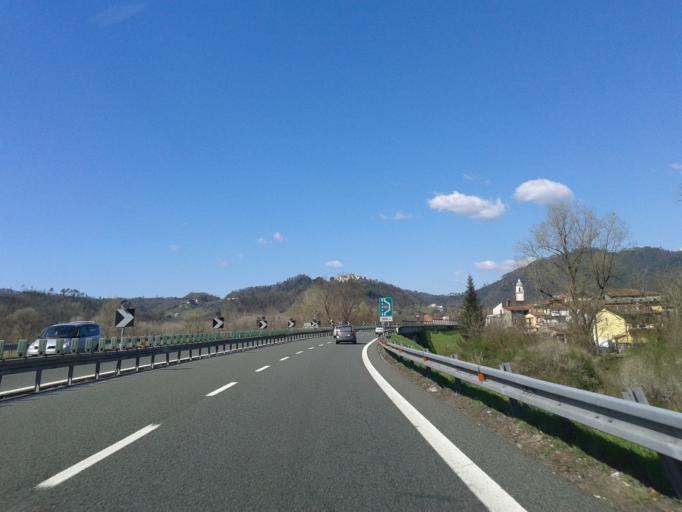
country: IT
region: Liguria
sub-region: Provincia di La Spezia
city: Beverino
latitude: 44.1983
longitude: 9.8147
